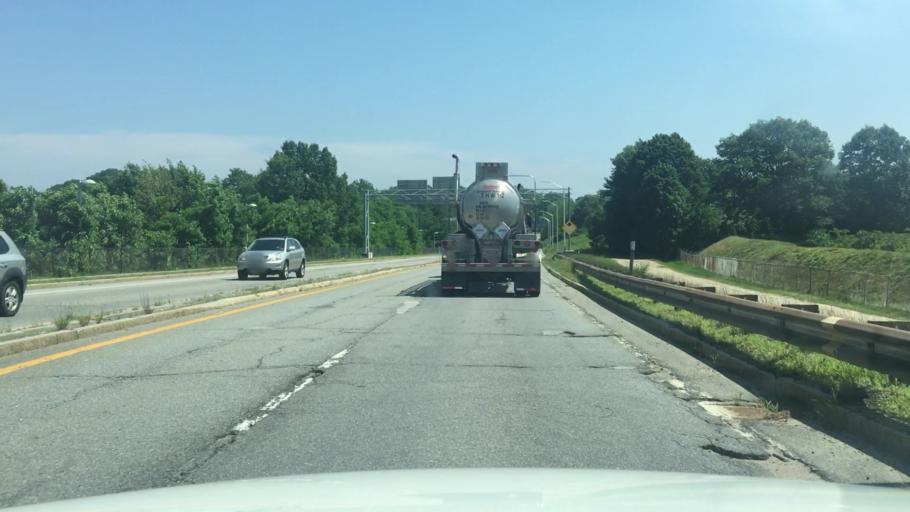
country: US
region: Maine
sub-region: Cumberland County
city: South Portland Gardens
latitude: 43.6374
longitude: -70.2921
